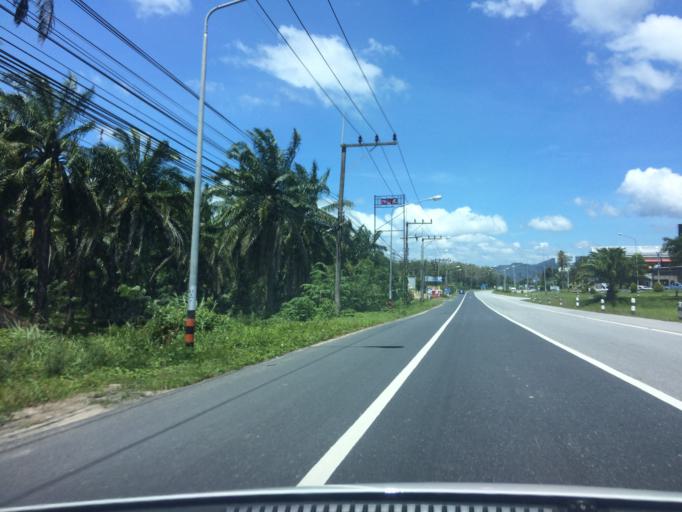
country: TH
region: Phangnga
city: Thai Mueang
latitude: 8.2446
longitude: 98.2976
